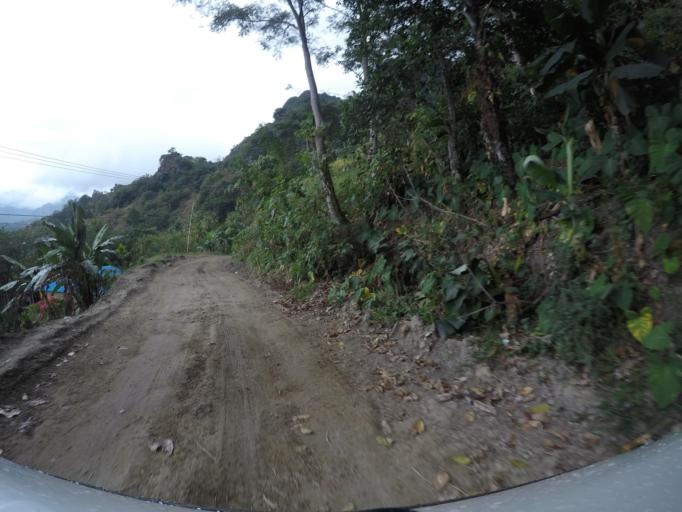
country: TL
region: Baucau
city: Baucau
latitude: -8.6393
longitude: 126.6408
